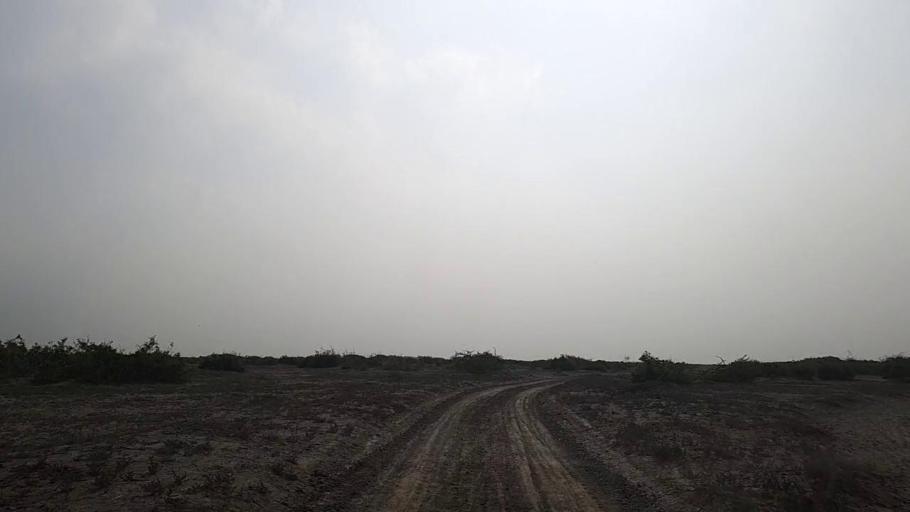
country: PK
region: Sindh
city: Gharo
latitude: 24.6728
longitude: 67.6435
